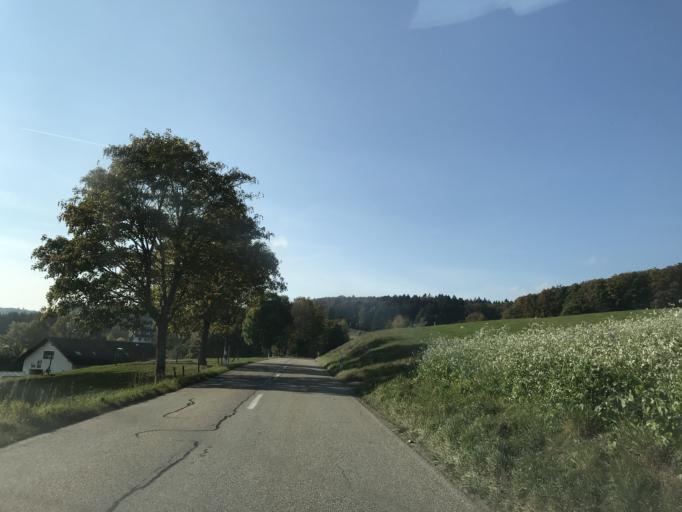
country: DE
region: Baden-Wuerttemberg
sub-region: Freiburg Region
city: Gorwihl
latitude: 47.6338
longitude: 8.0662
